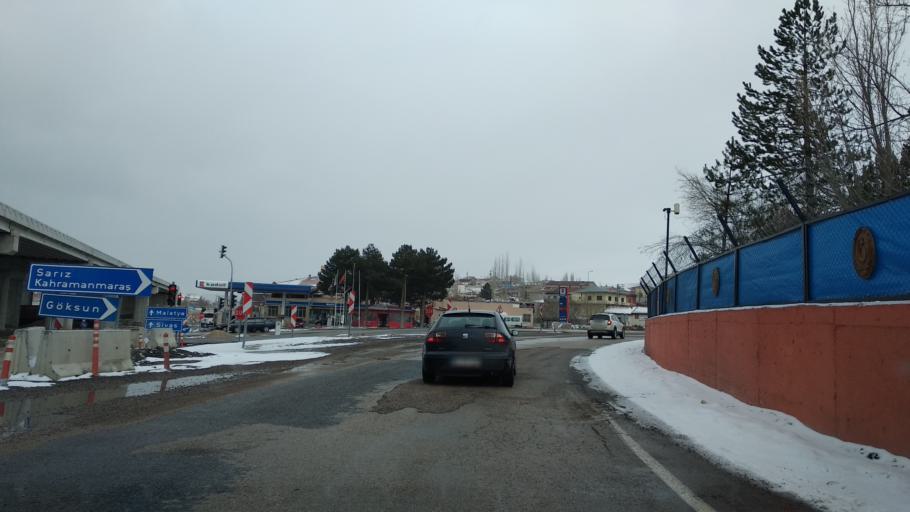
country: TR
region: Kayseri
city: Pinarbasi
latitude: 38.7281
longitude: 36.4010
